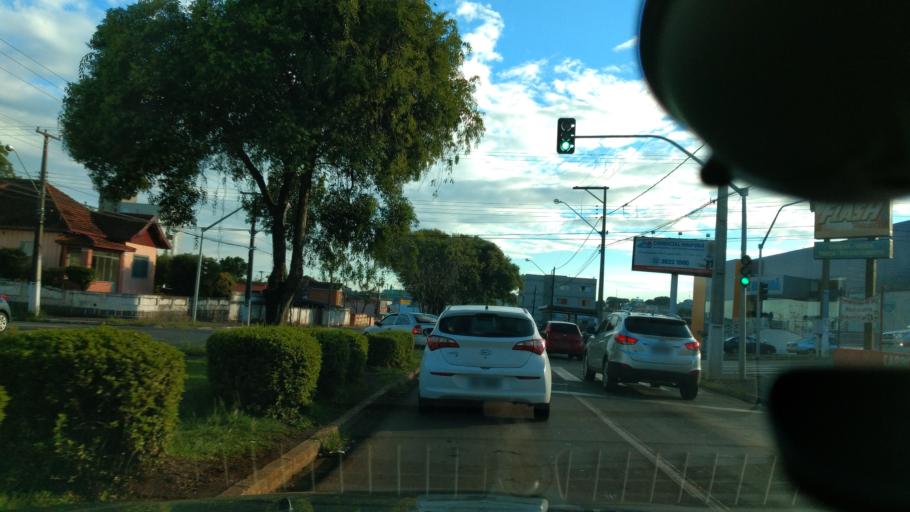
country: BR
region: Parana
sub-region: Guarapuava
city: Guarapuava
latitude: -25.3899
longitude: -51.4770
